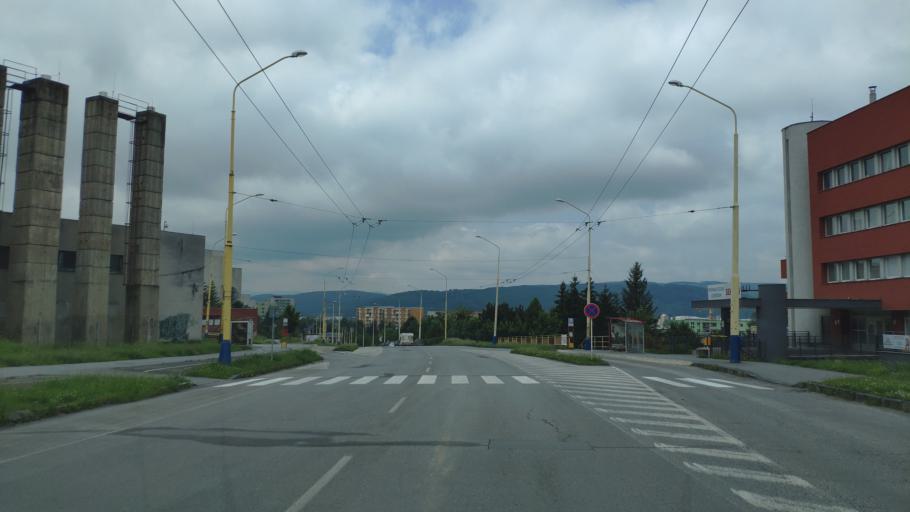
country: SK
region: Presovsky
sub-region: Okres Presov
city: Presov
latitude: 48.9924
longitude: 21.2718
